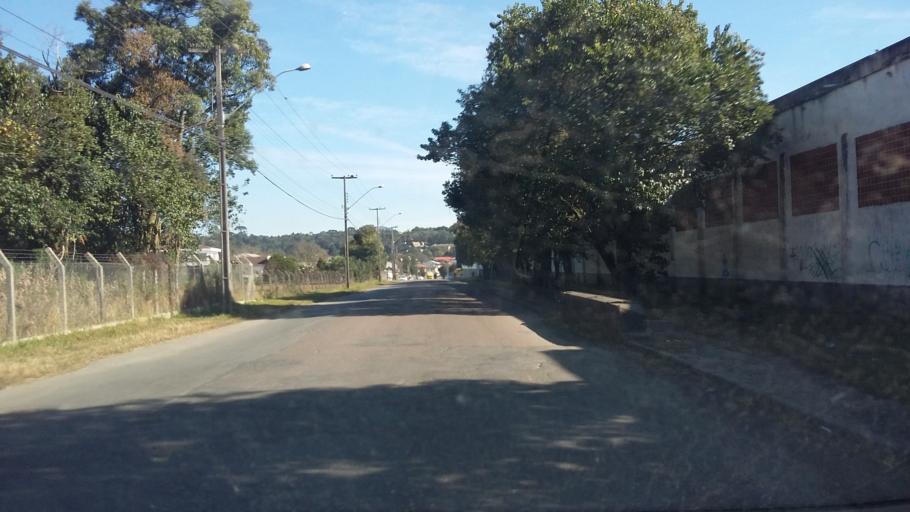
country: BR
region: Parana
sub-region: Campo Largo
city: Campo Largo
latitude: -25.4674
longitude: -49.5703
